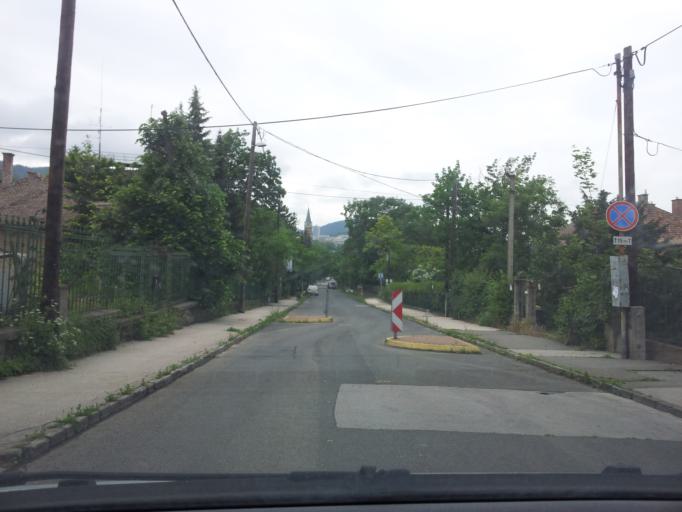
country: HU
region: Budapest
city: Budapest XII. keruelet
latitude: 47.5142
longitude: 18.9919
